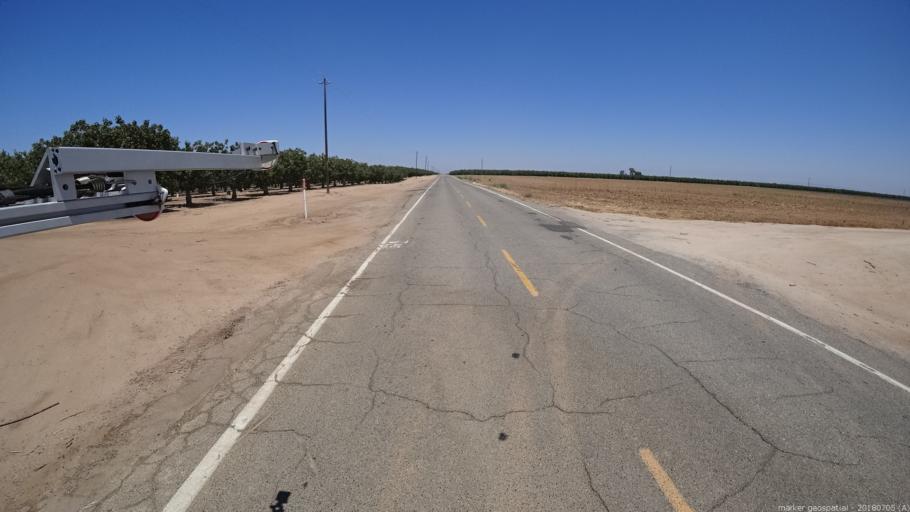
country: US
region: California
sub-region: Madera County
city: Madera Acres
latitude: 37.0688
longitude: -120.0746
